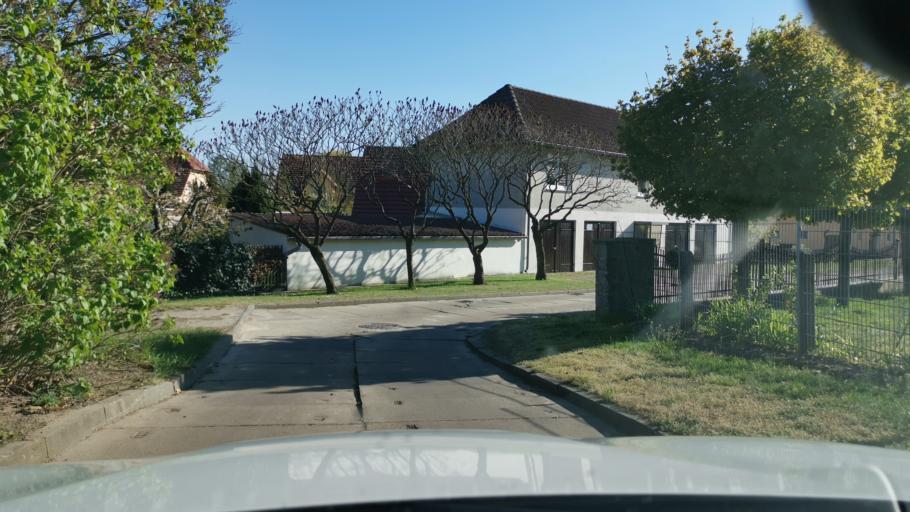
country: DE
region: Brandenburg
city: Juterbog
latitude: 52.0011
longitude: 13.0886
